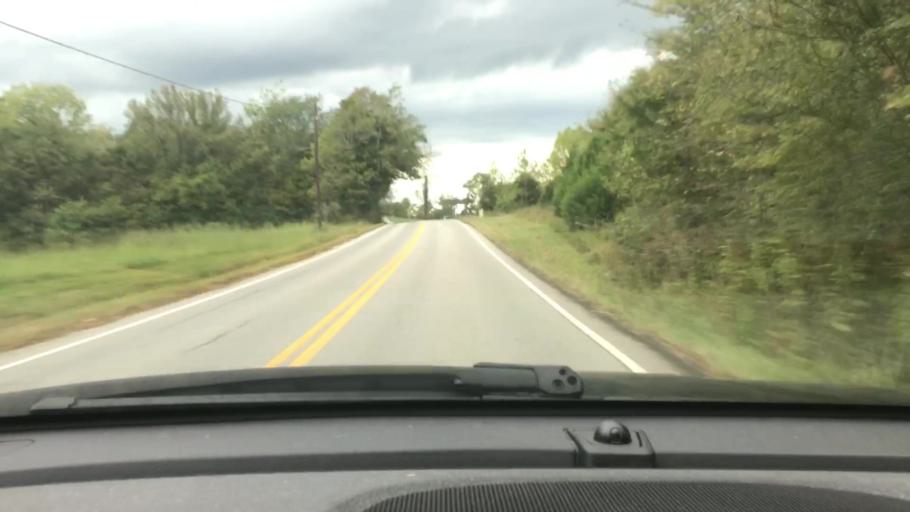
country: US
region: Tennessee
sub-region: Cheatham County
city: Ashland City
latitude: 36.2689
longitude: -87.2063
